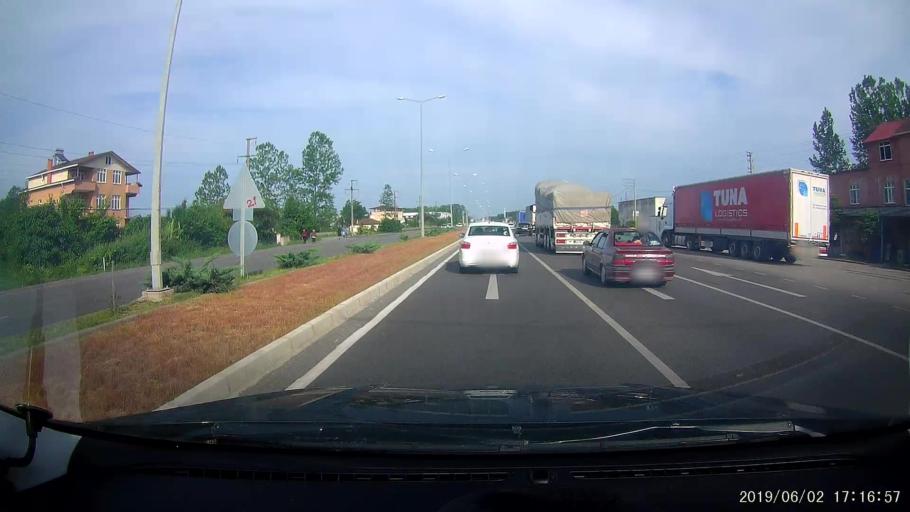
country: TR
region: Samsun
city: Dikbiyik
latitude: 41.2319
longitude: 36.5741
